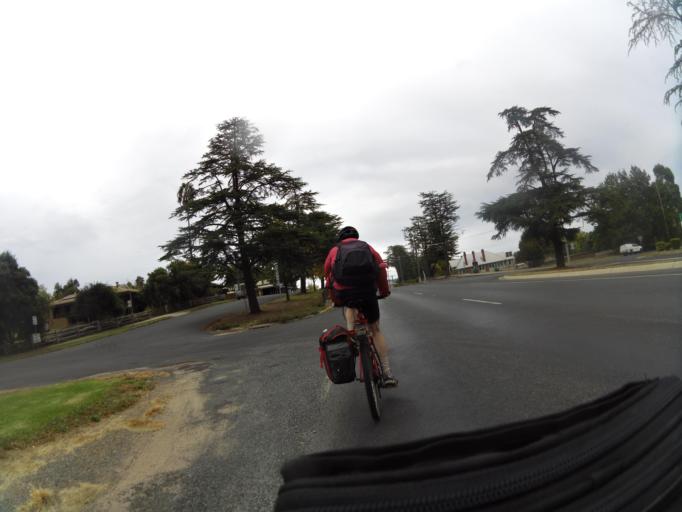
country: AU
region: New South Wales
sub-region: Snowy River
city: Jindabyne
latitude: -36.1936
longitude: 147.9087
